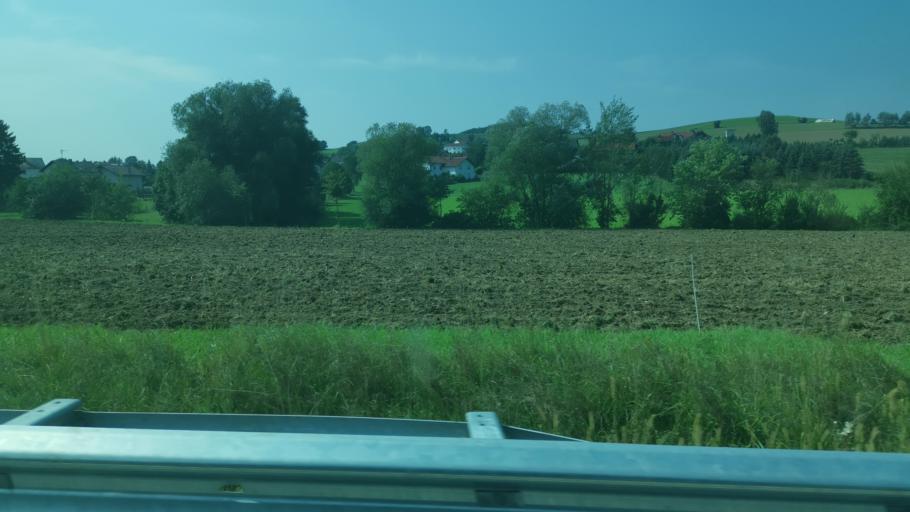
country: DE
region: Bavaria
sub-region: Upper Palatinate
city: Willmering
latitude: 49.2423
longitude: 12.6725
